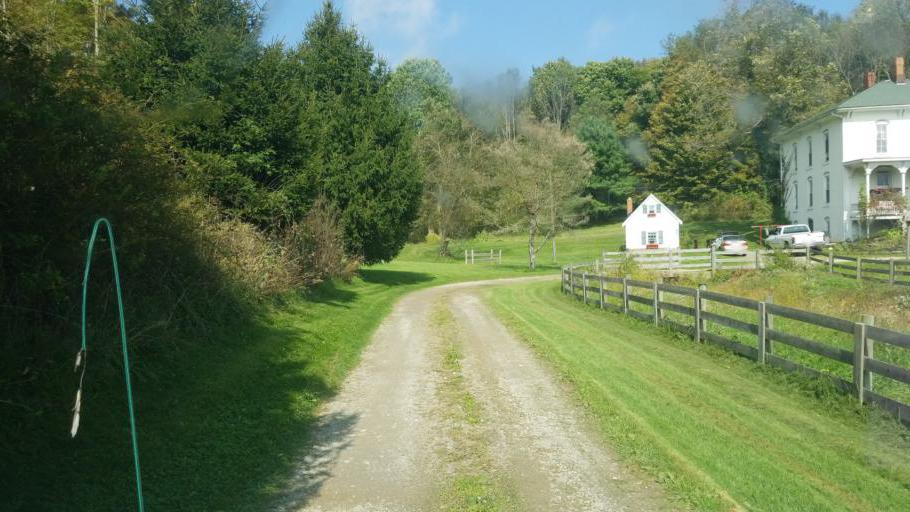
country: US
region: Ohio
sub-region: Sandusky County
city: Bellville
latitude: 40.5587
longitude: -82.4990
